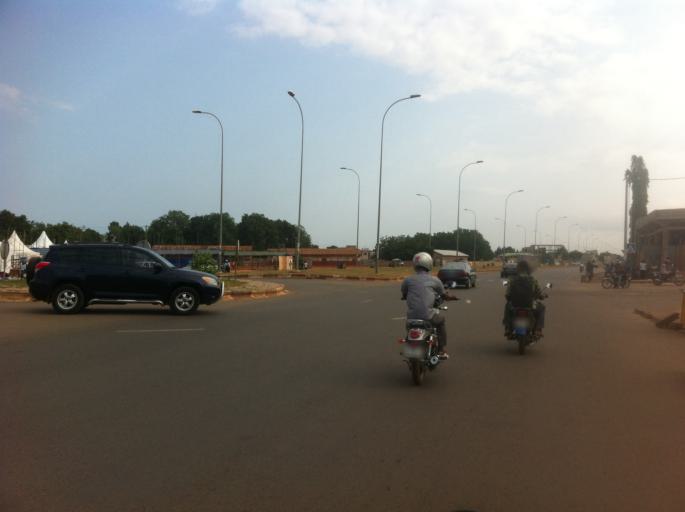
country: TG
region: Maritime
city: Lome
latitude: 6.2218
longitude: 1.1913
